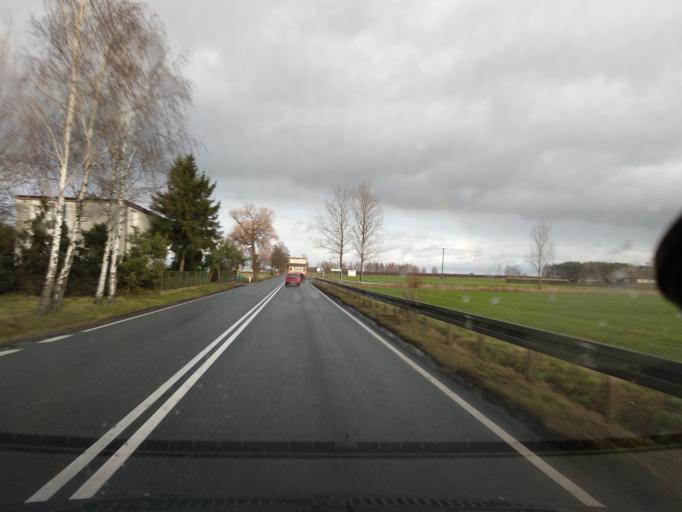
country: PL
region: Greater Poland Voivodeship
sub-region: Powiat koninski
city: Stare Miasto
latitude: 52.1386
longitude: 18.1894
